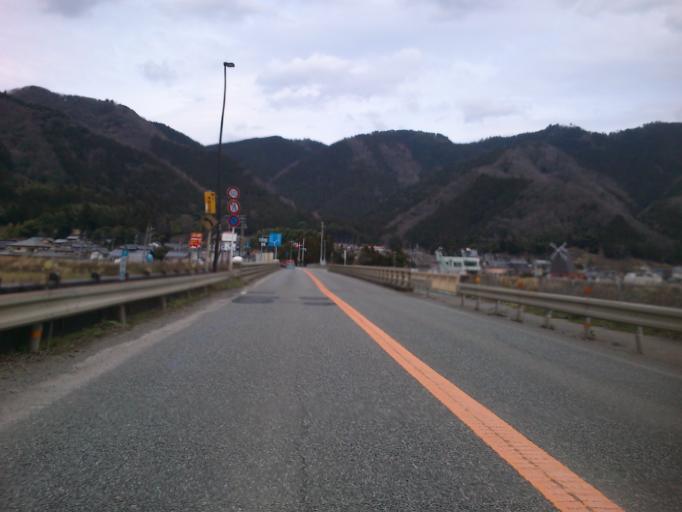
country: JP
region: Kyoto
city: Fukuchiyama
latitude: 35.3330
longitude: 135.0989
